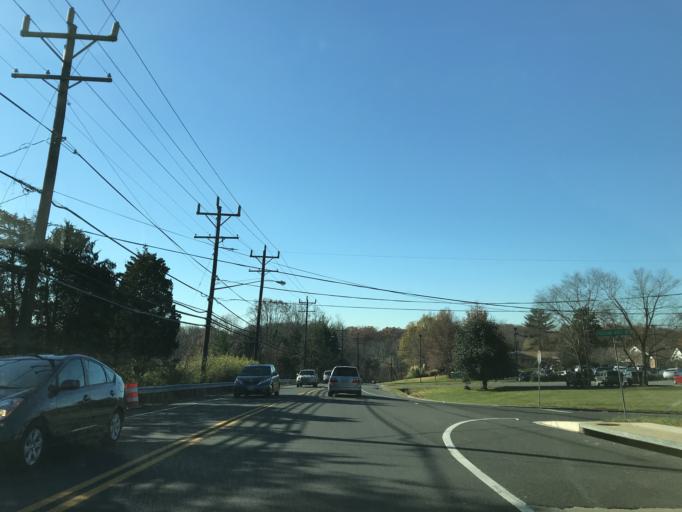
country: US
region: Maryland
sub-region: Montgomery County
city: Hillandale
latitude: 39.0343
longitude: -76.9498
